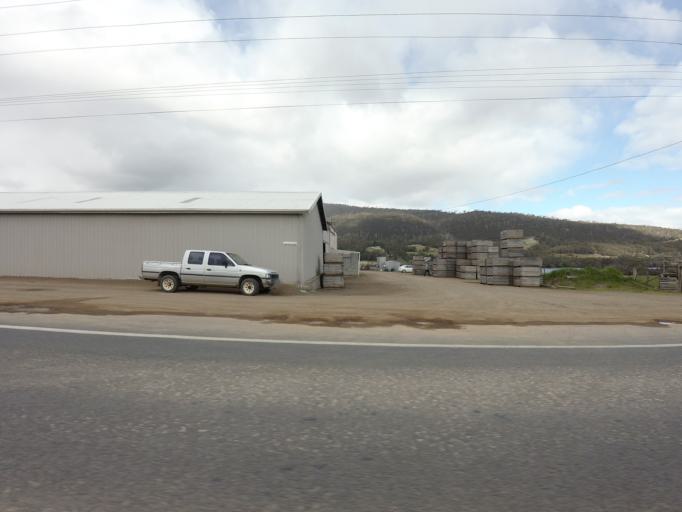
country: AU
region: Tasmania
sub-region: Huon Valley
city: Huonville
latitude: -43.0497
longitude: 147.0387
